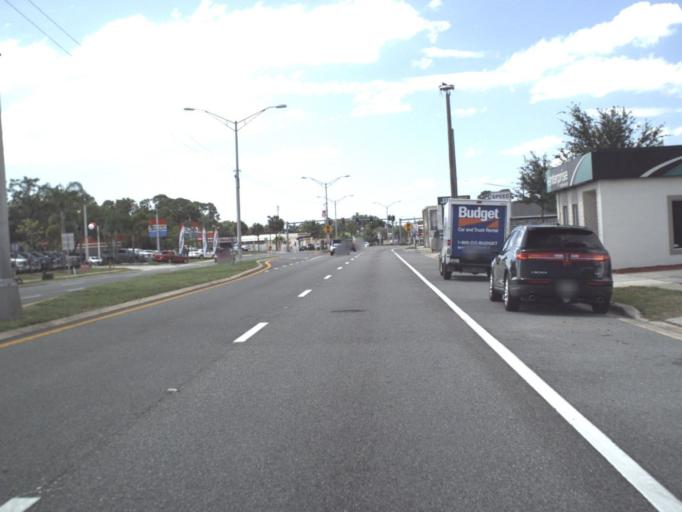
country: US
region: Florida
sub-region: Brevard County
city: Titusville
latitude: 28.5990
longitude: -80.8068
